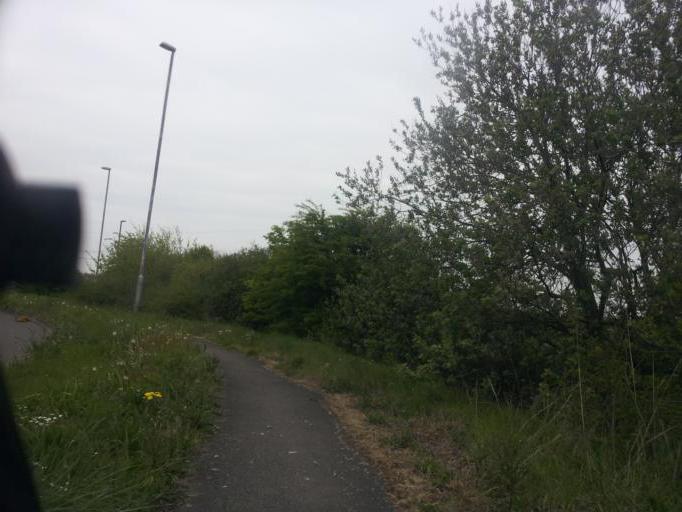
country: GB
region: England
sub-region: Medway
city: High Halstow
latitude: 51.4360
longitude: 0.5685
